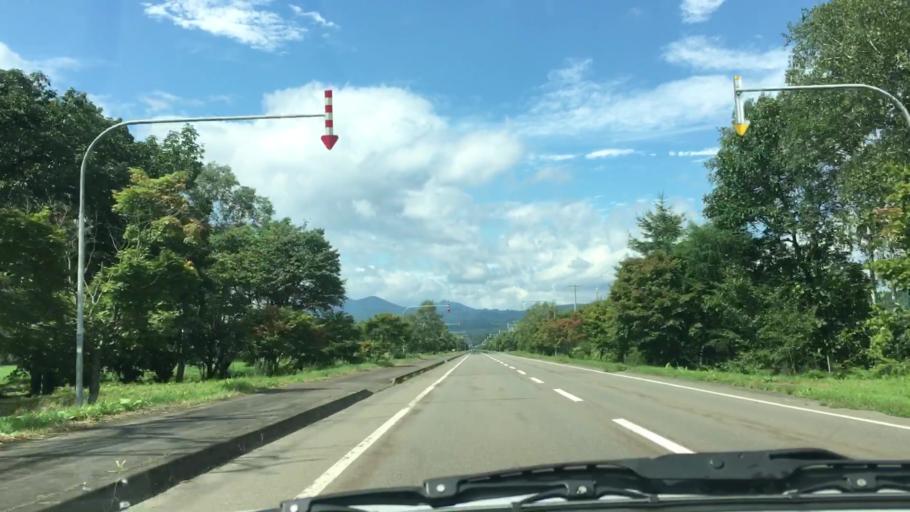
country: JP
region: Hokkaido
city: Otofuke
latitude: 43.3070
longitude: 143.3105
